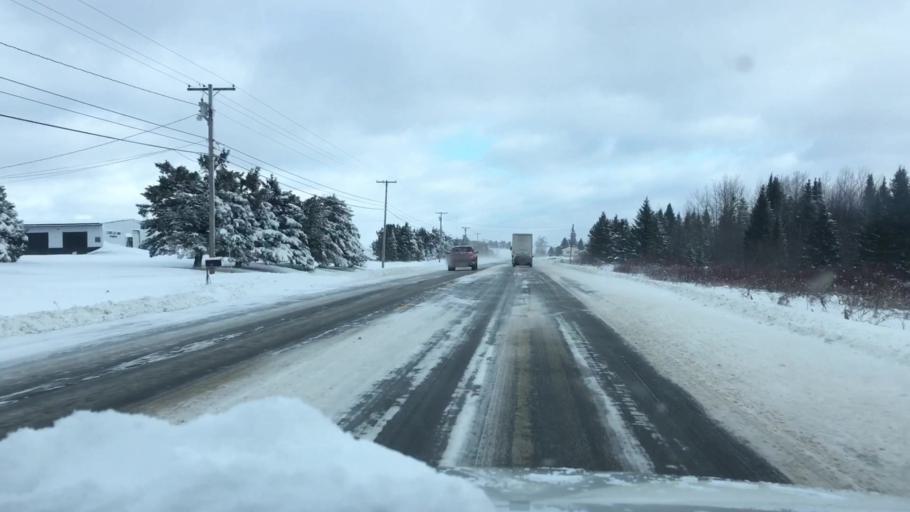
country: US
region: Maine
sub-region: Aroostook County
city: Presque Isle
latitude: 46.7372
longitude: -67.9988
